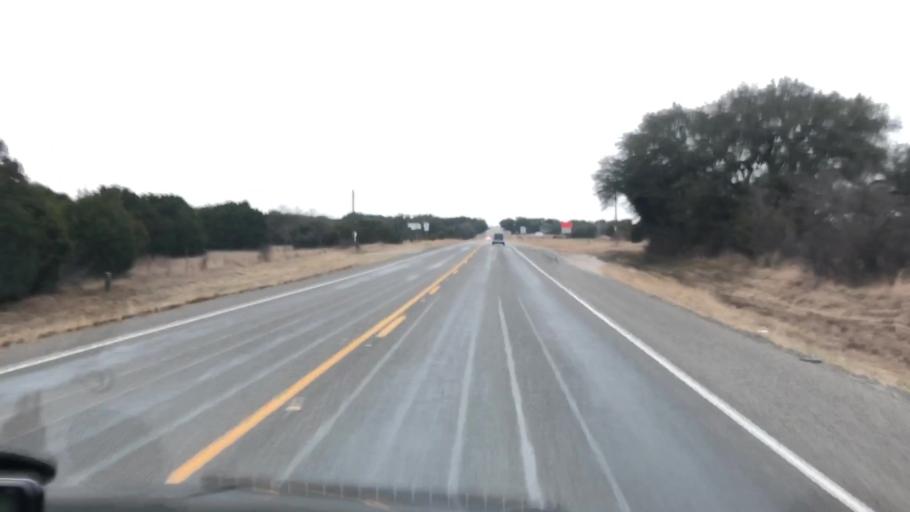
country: US
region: Texas
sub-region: Hamilton County
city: Hico
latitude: 31.9962
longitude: -98.0469
